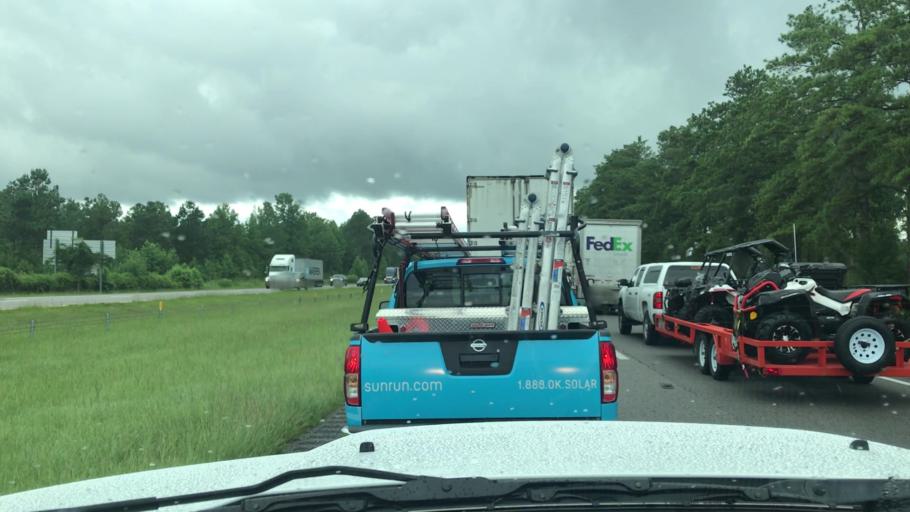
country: US
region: South Carolina
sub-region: Orangeburg County
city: Brookdale
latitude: 33.5655
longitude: -80.8304
